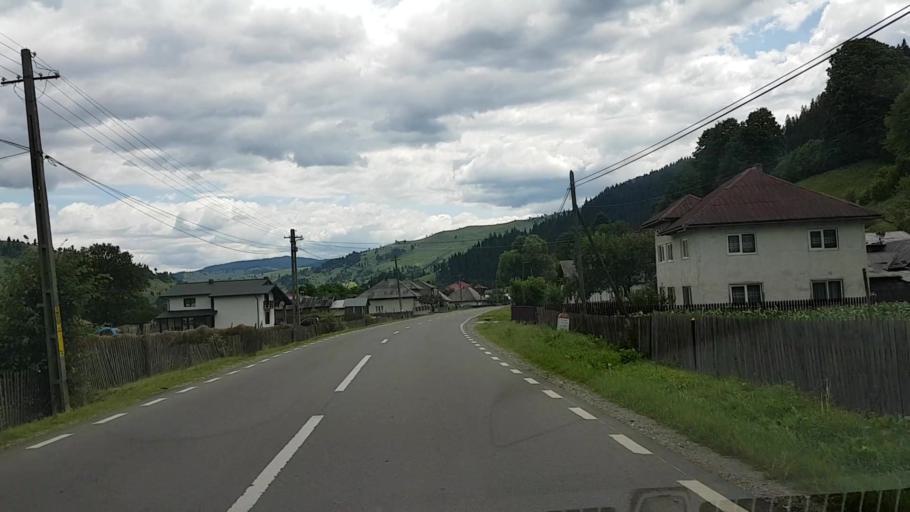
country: RO
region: Neamt
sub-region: Comuna Borca
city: Borca
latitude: 47.1897
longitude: 25.7723
